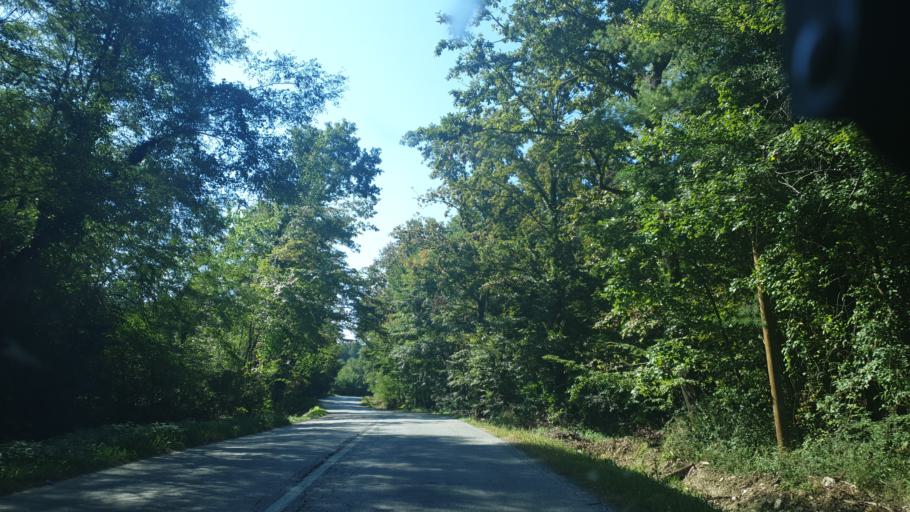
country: RS
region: Central Serbia
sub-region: Kolubarski Okrug
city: Lajkovac
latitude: 44.3128
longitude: 20.1840
